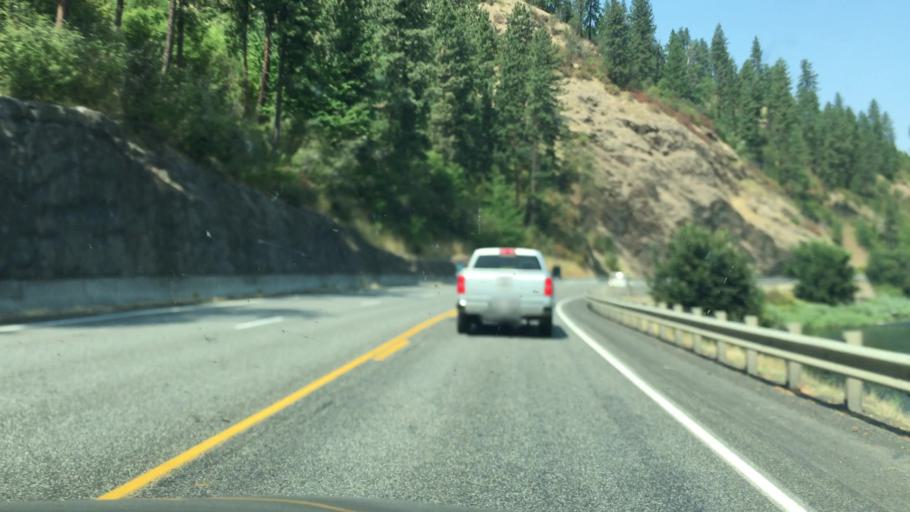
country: US
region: Idaho
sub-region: Nez Perce County
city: Lapwai
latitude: 46.5067
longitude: -116.5759
